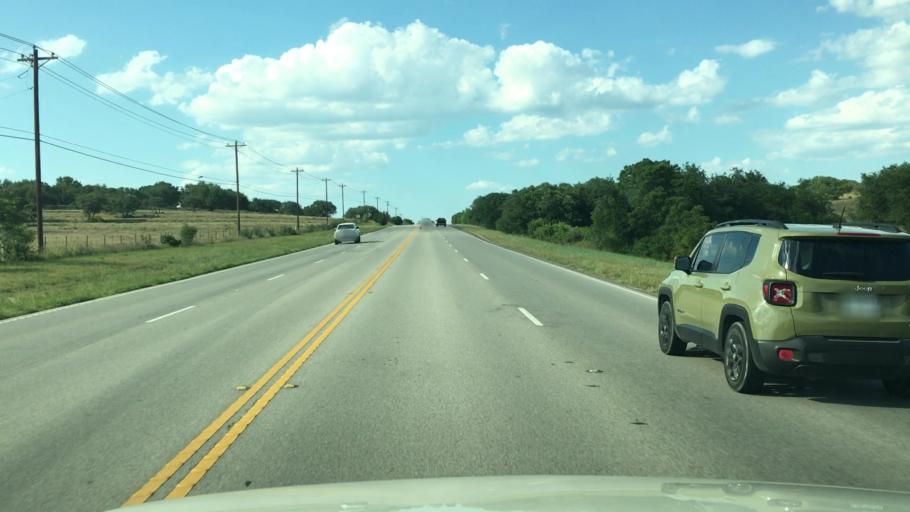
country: US
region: Texas
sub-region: Blanco County
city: Johnson City
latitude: 30.3706
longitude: -98.3747
